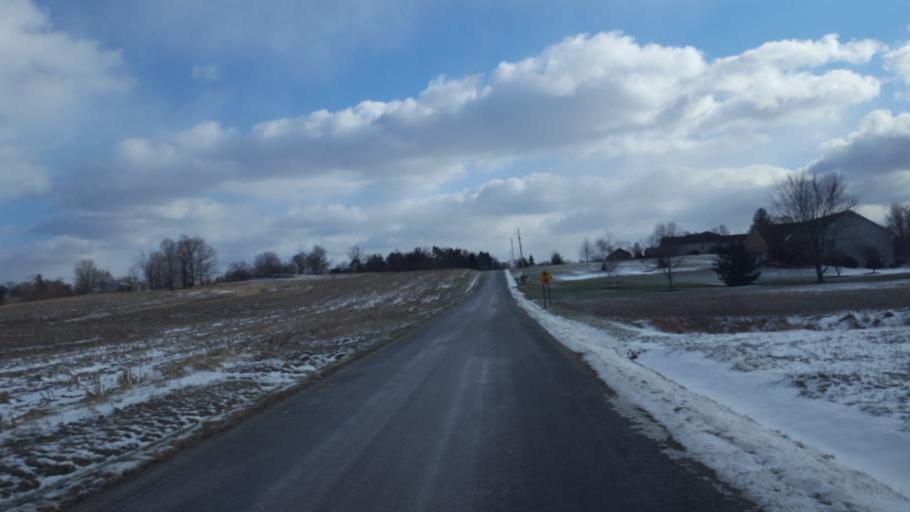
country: US
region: Ohio
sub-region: Crawford County
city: Galion
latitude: 40.7138
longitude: -82.7224
